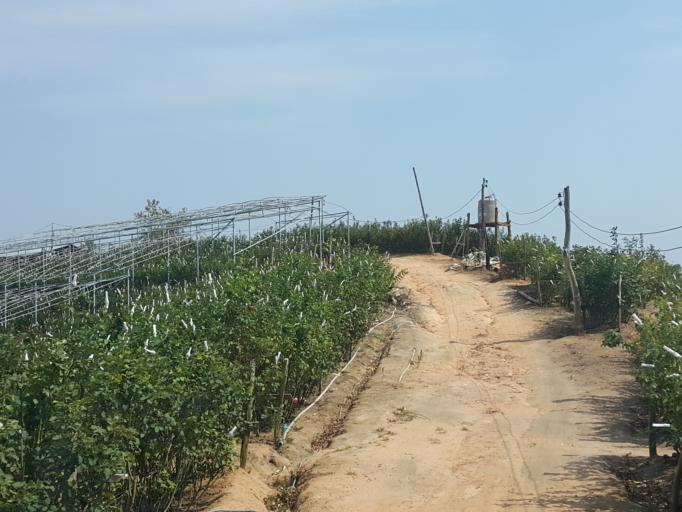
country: TH
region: Chiang Mai
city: Samoeng
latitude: 18.8838
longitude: 98.7965
